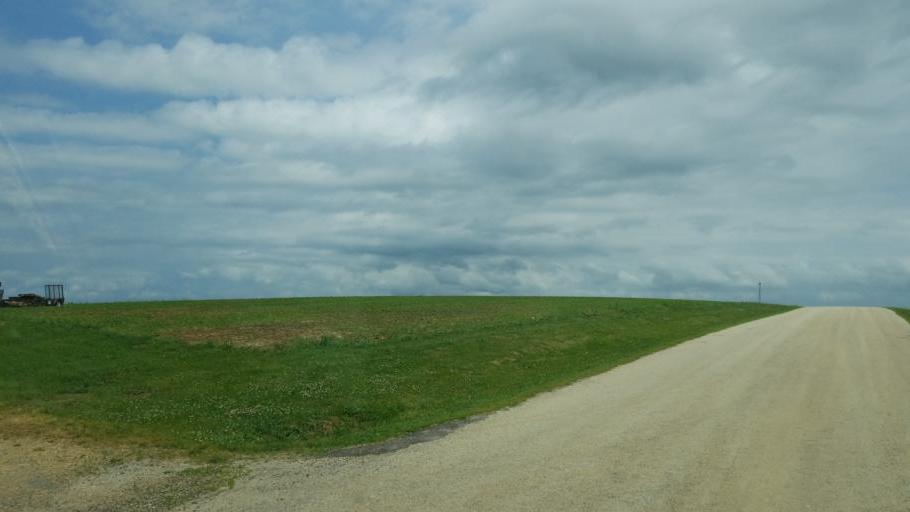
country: US
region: Wisconsin
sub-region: Monroe County
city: Cashton
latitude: 43.7051
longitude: -90.6223
